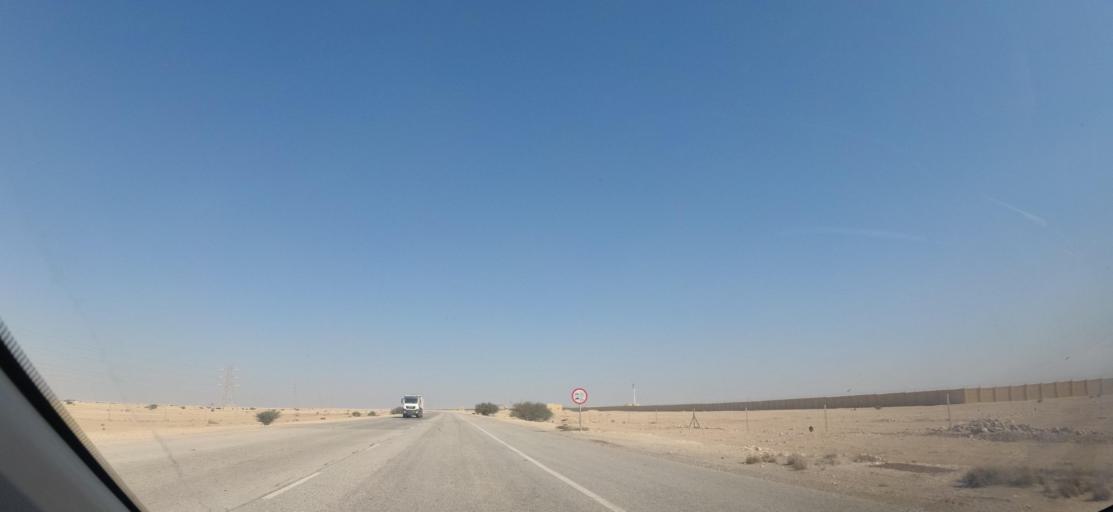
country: QA
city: Al Jumayliyah
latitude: 25.4834
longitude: 50.9678
